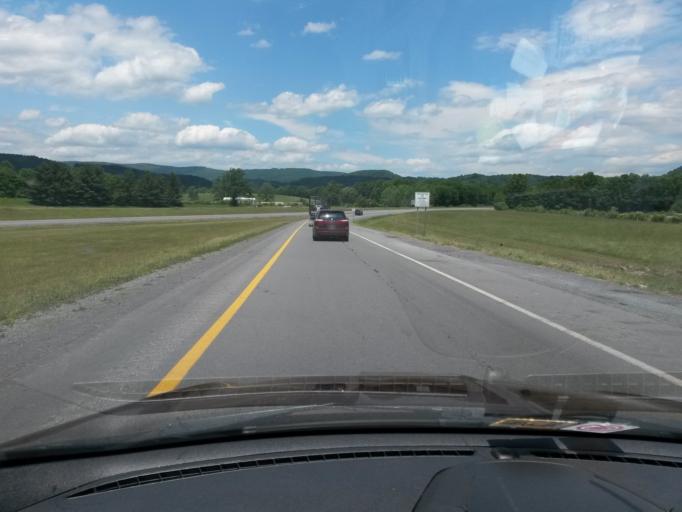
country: US
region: West Virginia
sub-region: Greenbrier County
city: Rainelle
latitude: 37.9028
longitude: -80.6323
